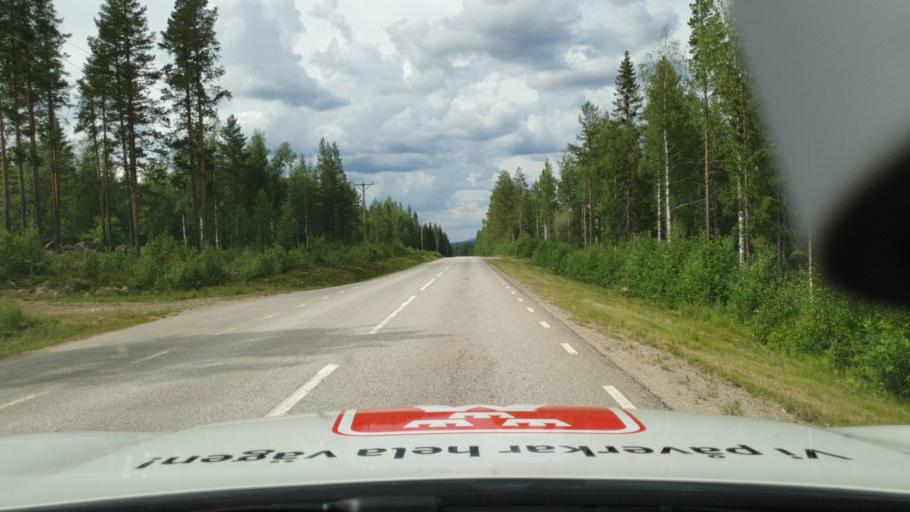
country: NO
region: Hedmark
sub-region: Trysil
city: Innbygda
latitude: 61.0013
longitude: 12.4866
